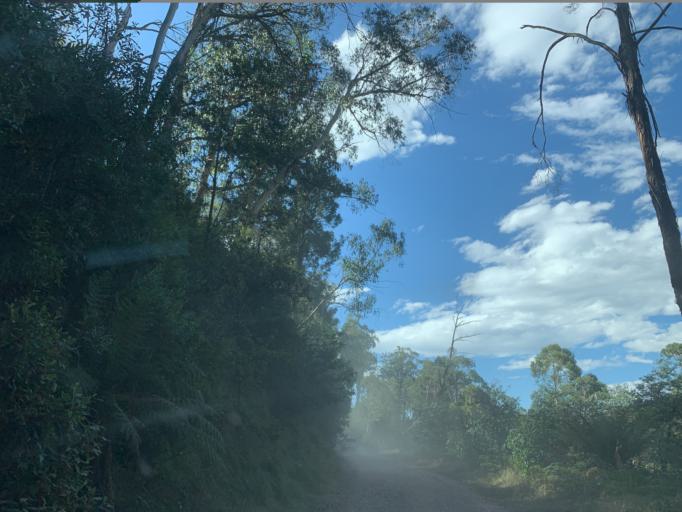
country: AU
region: Victoria
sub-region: Mansfield
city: Mansfield
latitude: -37.0942
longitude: 146.5184
